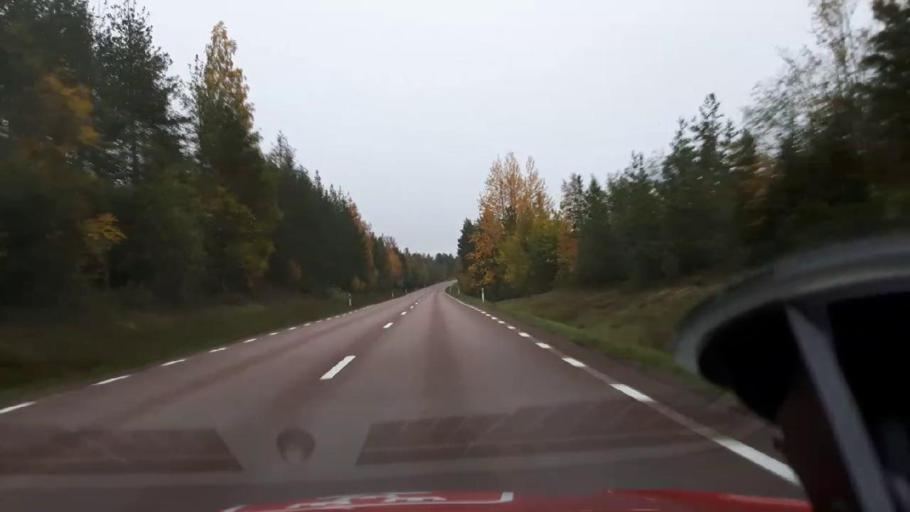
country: SE
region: Jaemtland
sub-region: Bergs Kommun
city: Hoverberg
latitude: 62.5186
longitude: 14.4486
